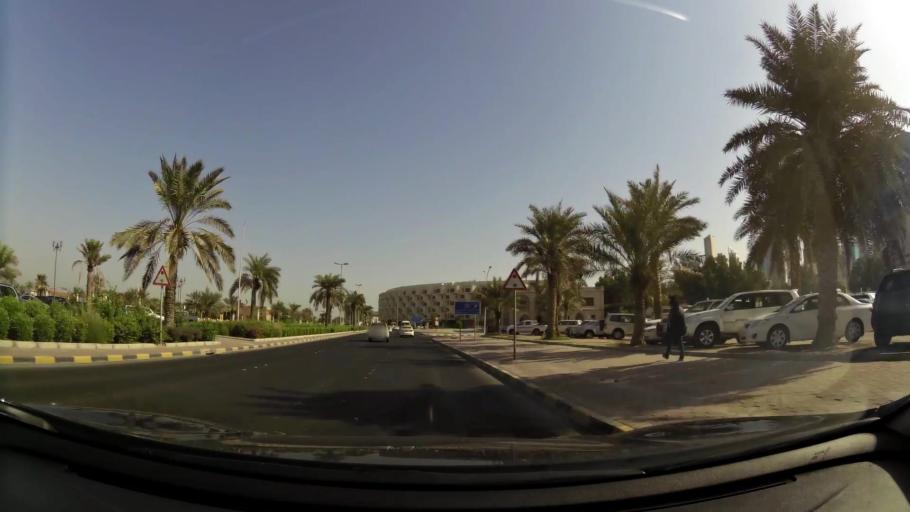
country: KW
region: Al Asimah
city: Kuwait City
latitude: 29.3669
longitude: 47.9609
